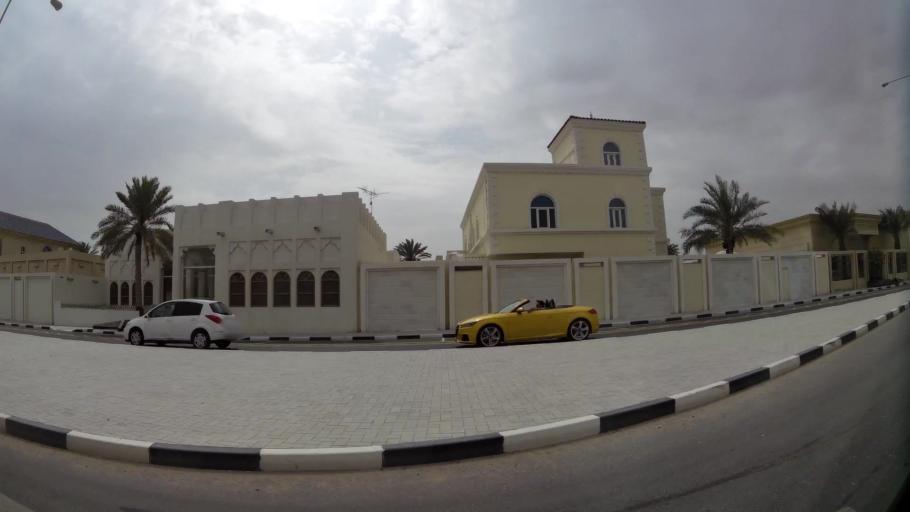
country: QA
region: Baladiyat ar Rayyan
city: Ar Rayyan
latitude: 25.3461
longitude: 51.4683
